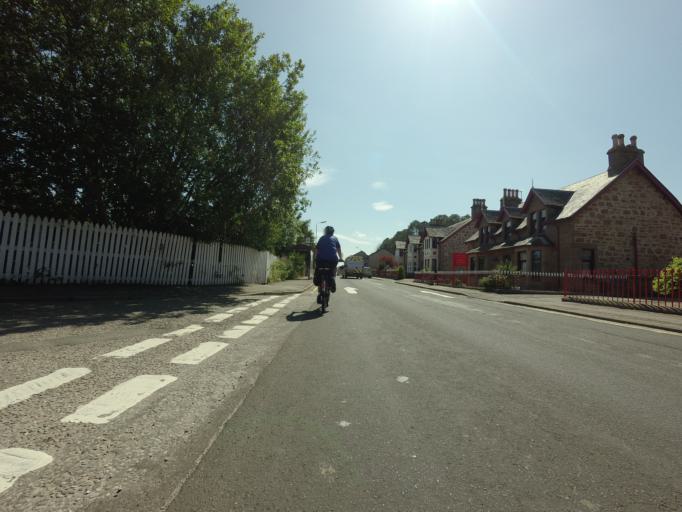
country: GB
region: Scotland
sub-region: Highland
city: Dingwall
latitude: 57.5940
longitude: -4.4233
